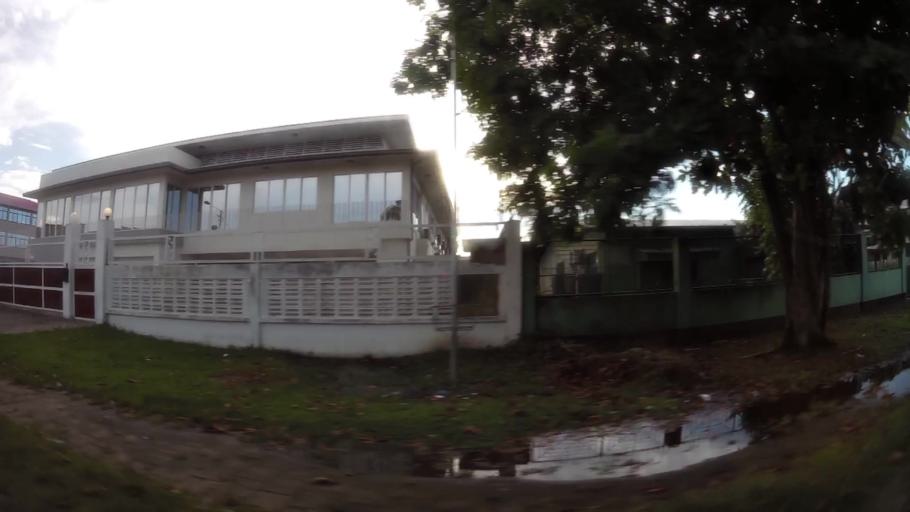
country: SR
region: Paramaribo
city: Paramaribo
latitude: 5.8312
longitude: -55.1828
